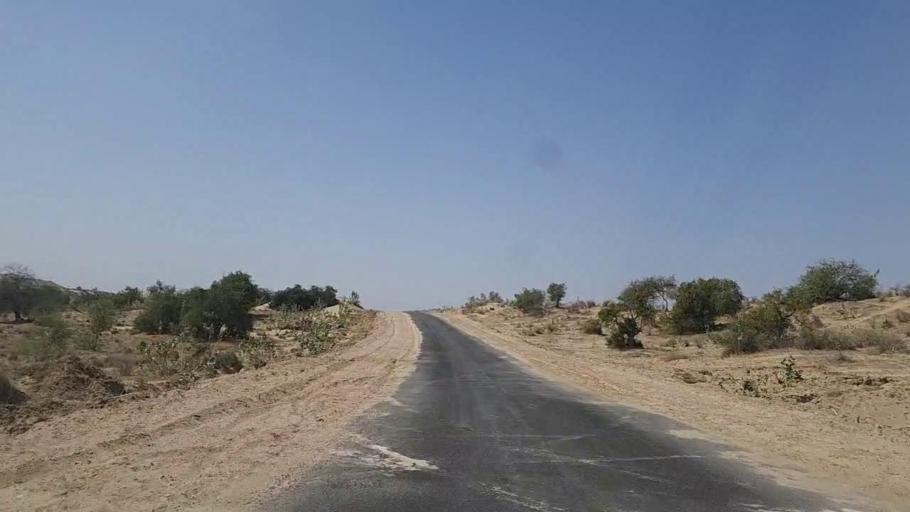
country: PK
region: Sindh
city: Diplo
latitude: 24.5784
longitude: 69.4937
